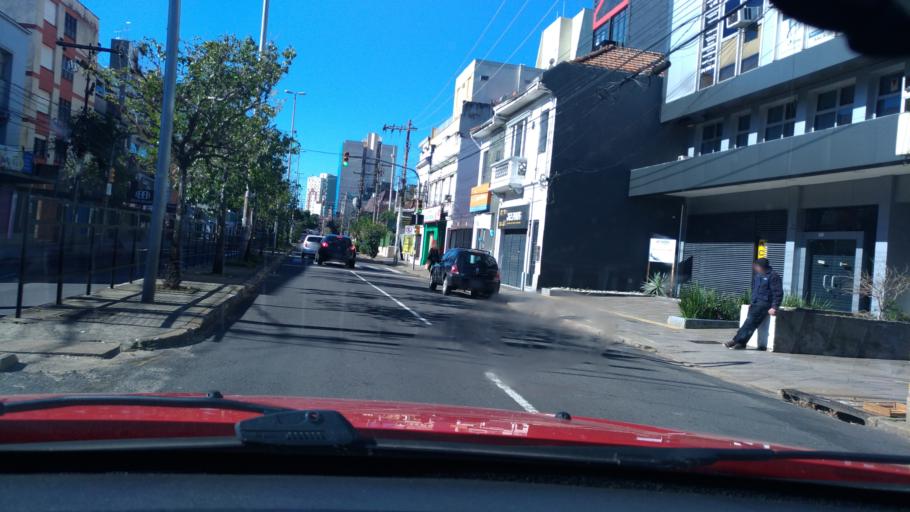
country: BR
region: Rio Grande do Sul
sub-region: Porto Alegre
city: Porto Alegre
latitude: -30.0220
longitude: -51.2085
